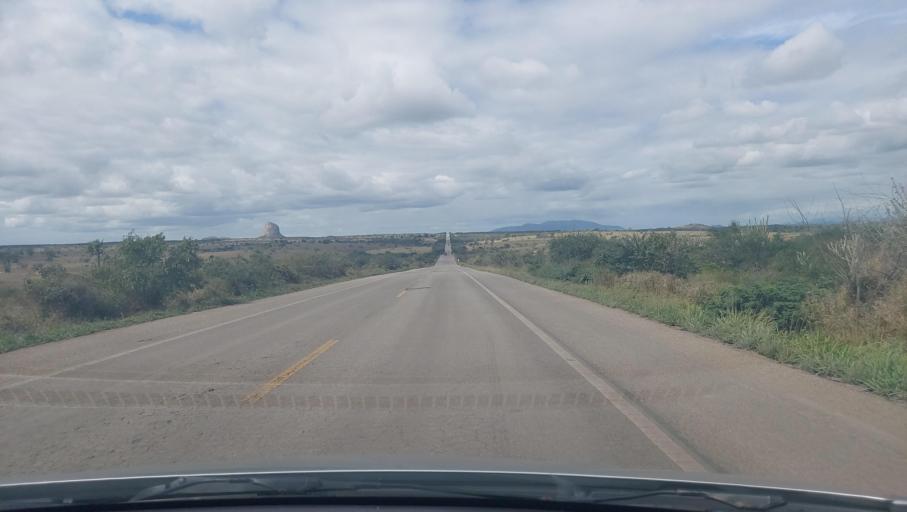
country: BR
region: Bahia
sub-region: Itaberaba
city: Itaberaba
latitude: -12.5208
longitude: -40.1375
